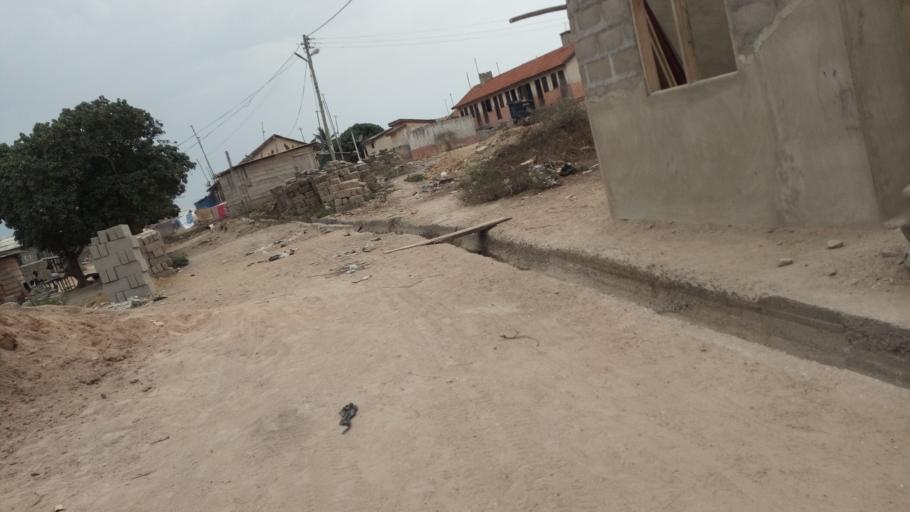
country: GH
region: Central
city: Winneba
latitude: 5.3346
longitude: -0.6208
